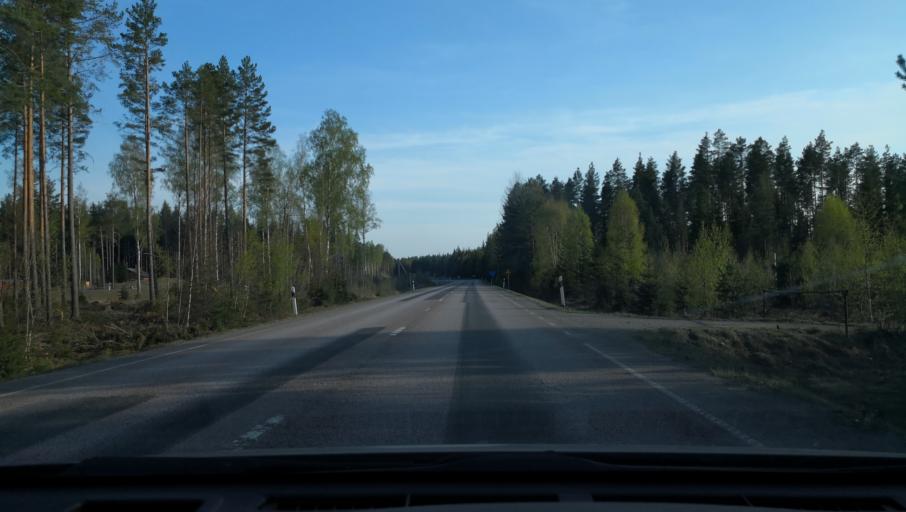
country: SE
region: Uppsala
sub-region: Heby Kommun
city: Heby
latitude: 59.9715
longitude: 16.8359
